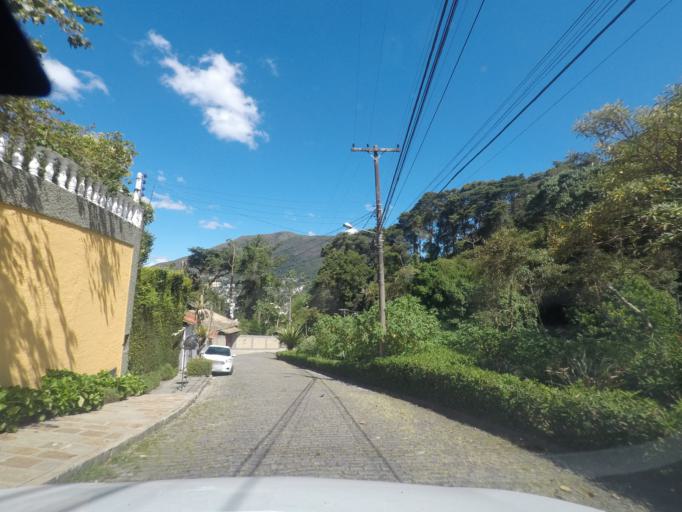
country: BR
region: Rio de Janeiro
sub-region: Teresopolis
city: Teresopolis
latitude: -22.4336
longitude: -42.9844
